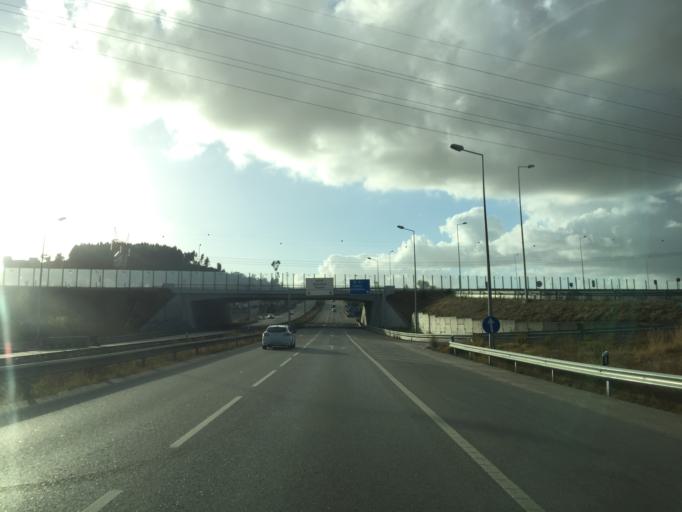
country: PT
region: Coimbra
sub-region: Coimbra
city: Coimbra
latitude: 40.2014
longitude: -8.4868
